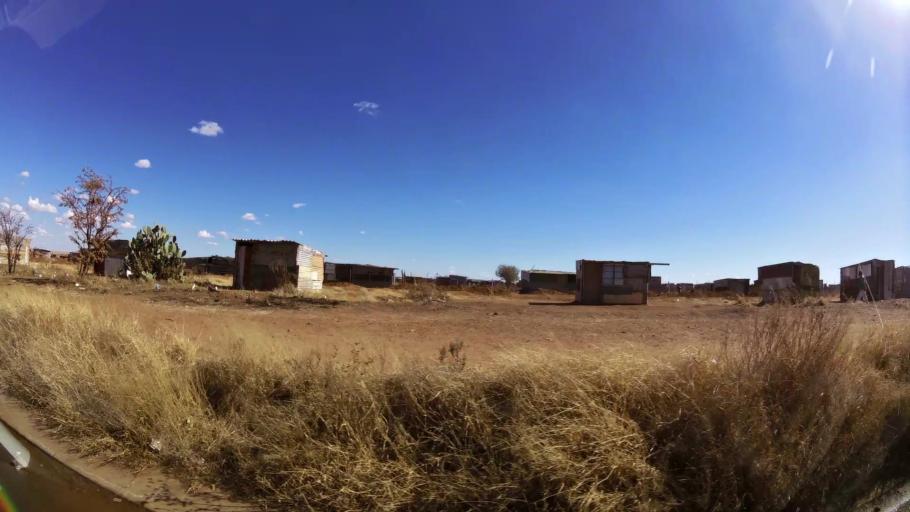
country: ZA
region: North-West
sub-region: Dr Kenneth Kaunda District Municipality
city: Klerksdorp
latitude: -26.8747
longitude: 26.5643
